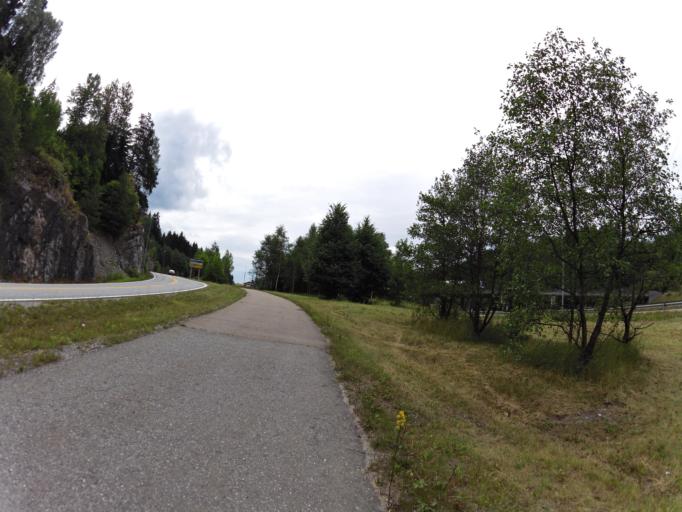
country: NO
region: Akershus
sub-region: As
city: As
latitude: 59.7081
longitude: 10.7384
